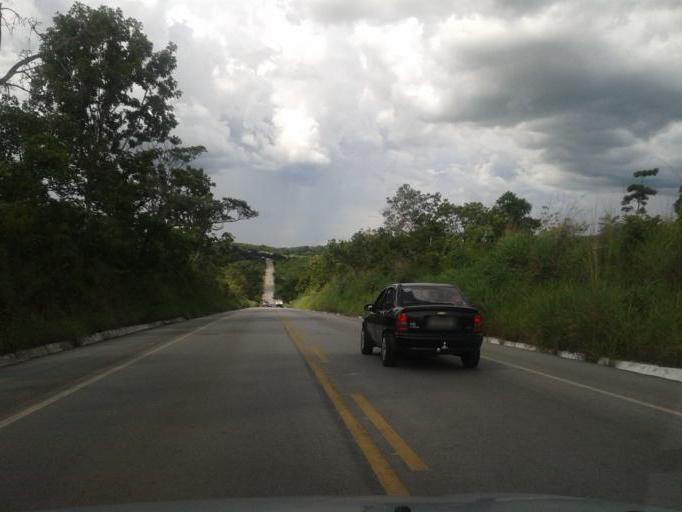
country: BR
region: Goias
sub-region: Goias
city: Goias
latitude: -15.8774
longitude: -50.0973
